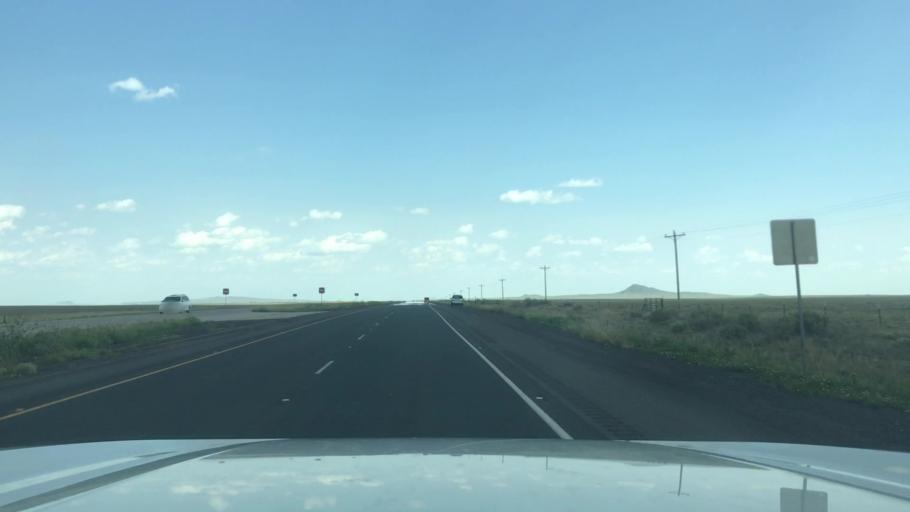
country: US
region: New Mexico
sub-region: Union County
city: Clayton
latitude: 36.6329
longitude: -103.7167
